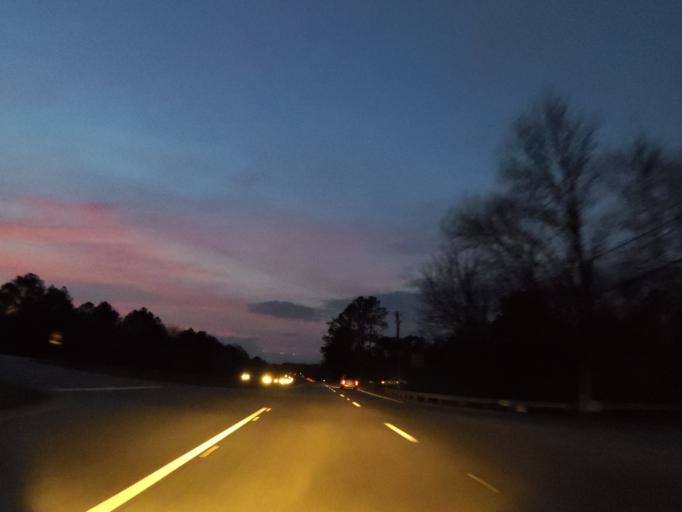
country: US
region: Tennessee
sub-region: Polk County
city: Benton
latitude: 35.1320
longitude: -84.7405
